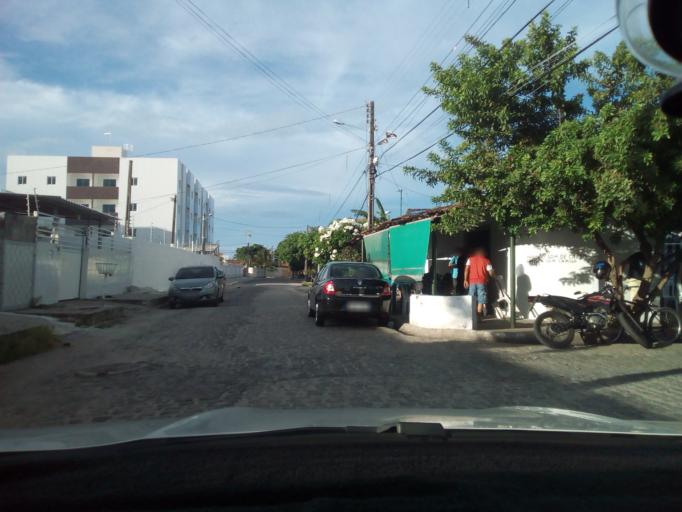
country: BR
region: Paraiba
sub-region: Joao Pessoa
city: Joao Pessoa
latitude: -7.1709
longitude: -34.8601
